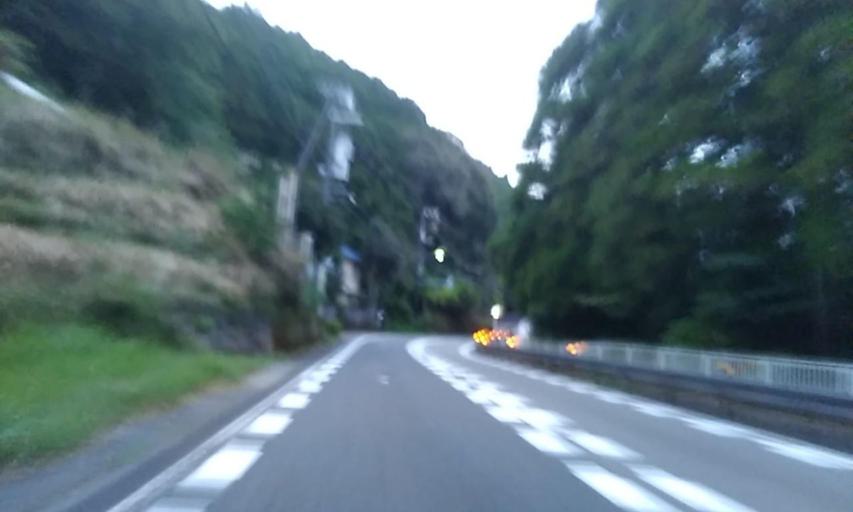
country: JP
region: Wakayama
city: Shingu
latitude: 33.7387
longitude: 135.9391
